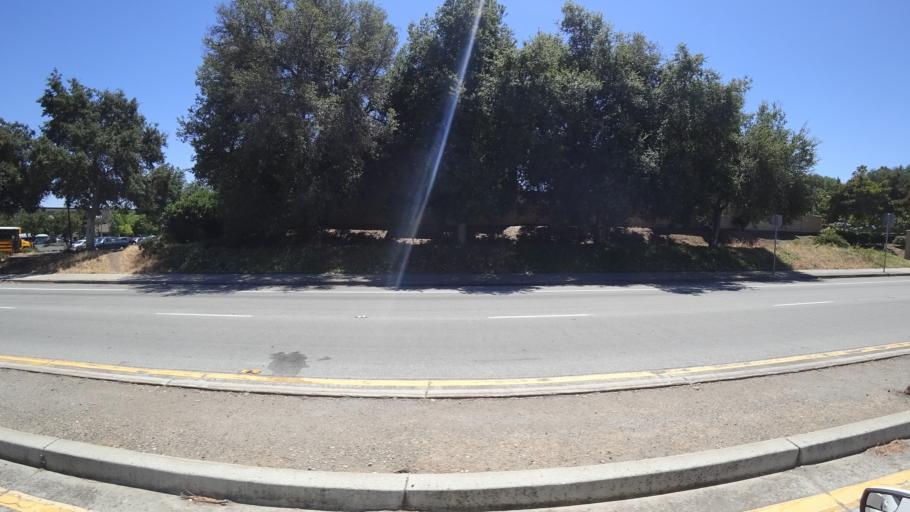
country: US
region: California
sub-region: Santa Clara County
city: Seven Trees
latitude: 37.2584
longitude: -121.8620
